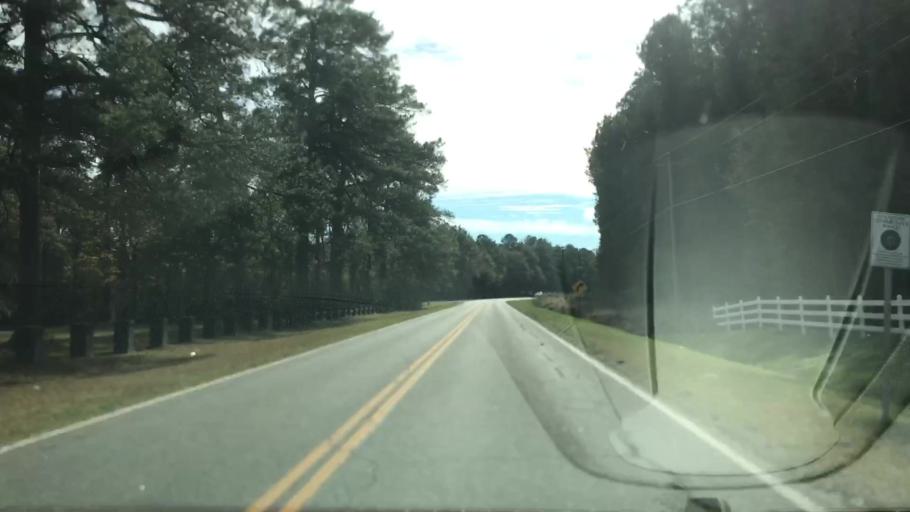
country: US
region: South Carolina
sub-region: Colleton County
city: Walterboro
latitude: 32.8724
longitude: -80.6151
